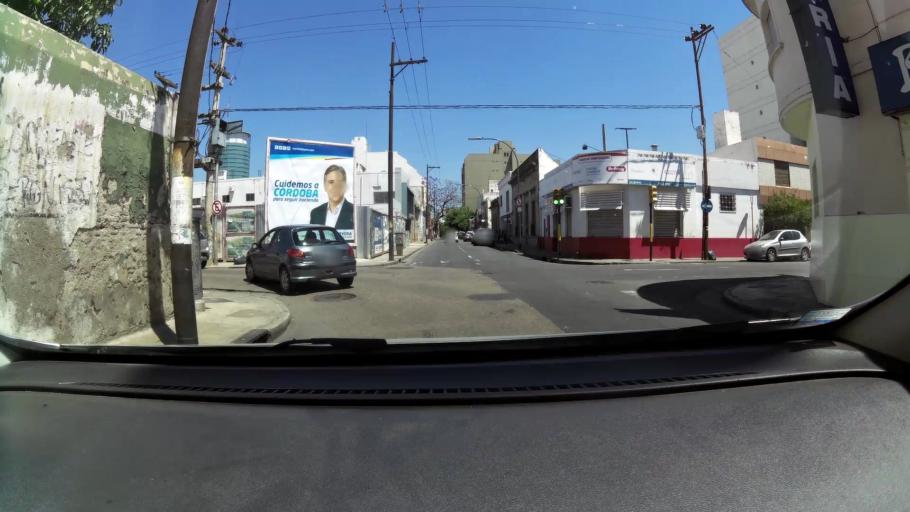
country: AR
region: Cordoba
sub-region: Departamento de Capital
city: Cordoba
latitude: -31.4128
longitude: -64.1993
